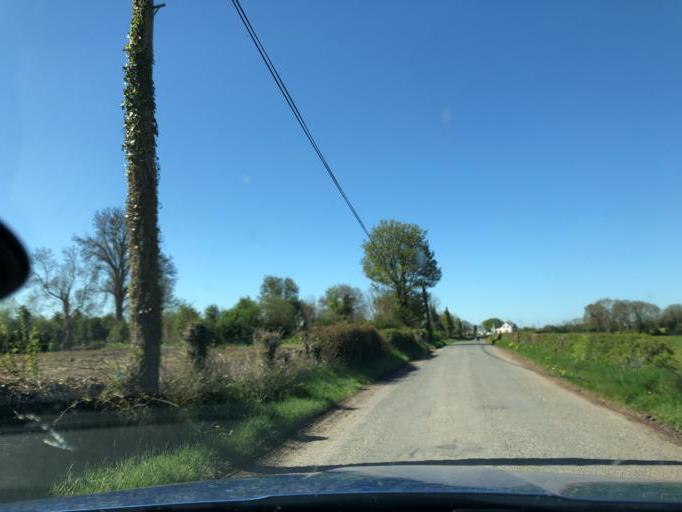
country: IE
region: Connaught
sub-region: County Galway
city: Portumna
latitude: 53.1846
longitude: -8.1680
